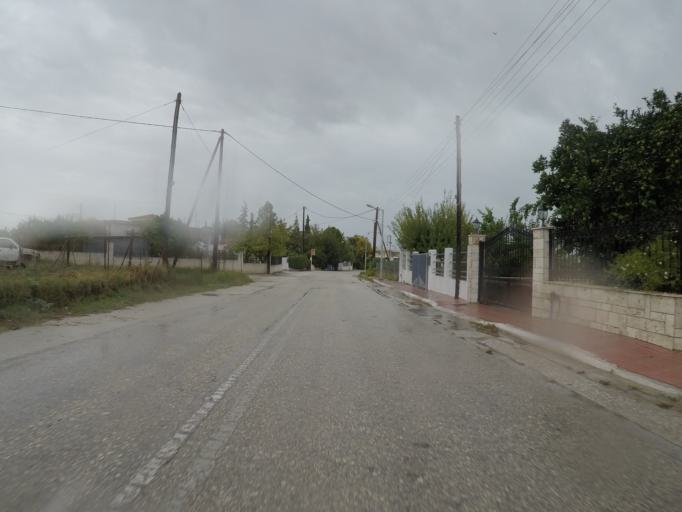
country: GR
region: Peloponnese
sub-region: Nomos Korinthias
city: Arkhaia Korinthos
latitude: 37.9049
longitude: 22.8846
